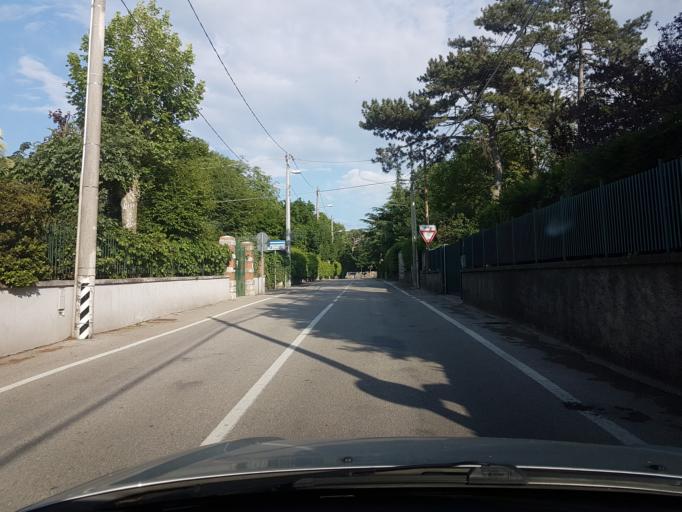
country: IT
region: Friuli Venezia Giulia
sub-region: Provincia di Trieste
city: Villa Opicina
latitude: 45.6860
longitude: 13.7840
